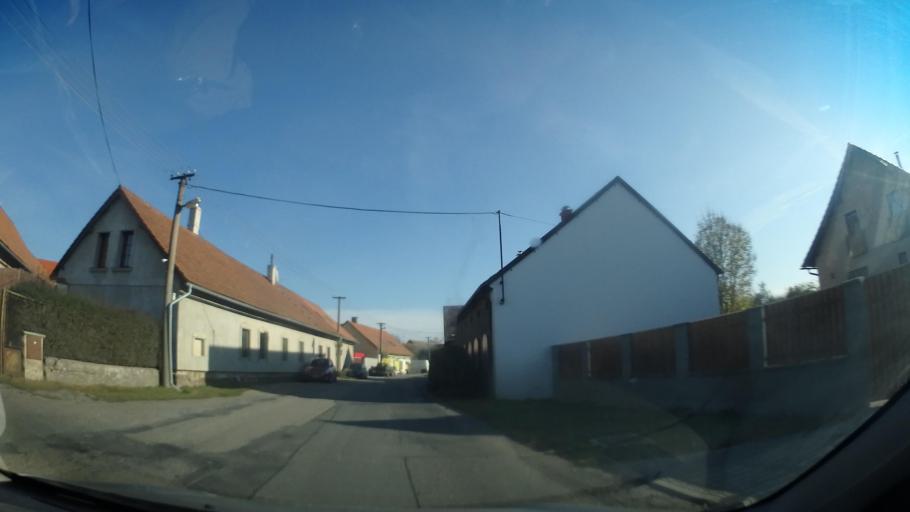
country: CZ
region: Central Bohemia
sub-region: Okres Praha-Vychod
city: Strancice
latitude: 49.9587
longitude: 14.6866
